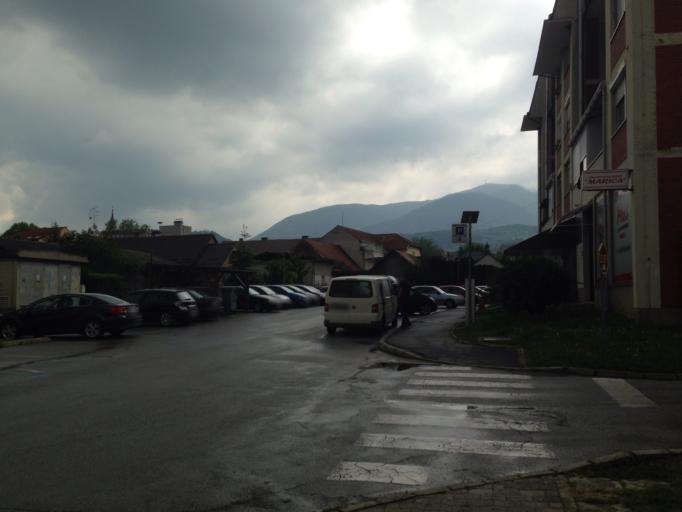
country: HR
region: Varazdinska
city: Ivanec
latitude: 46.2251
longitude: 16.1225
